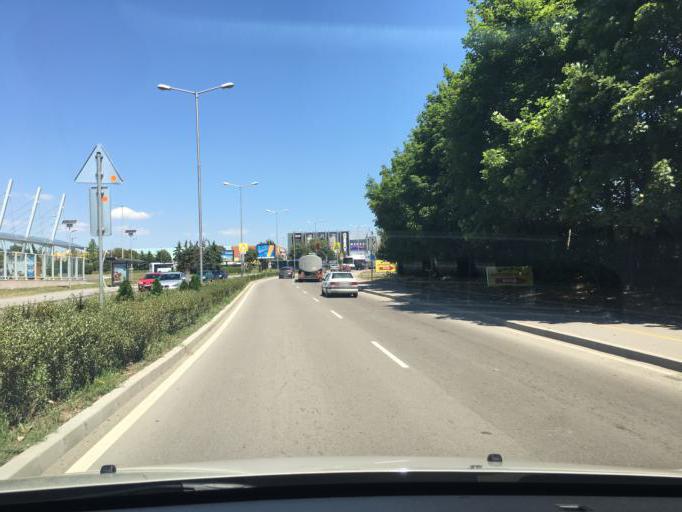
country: BG
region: Burgas
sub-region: Obshtina Burgas
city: Burgas
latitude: 42.5192
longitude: 27.4385
